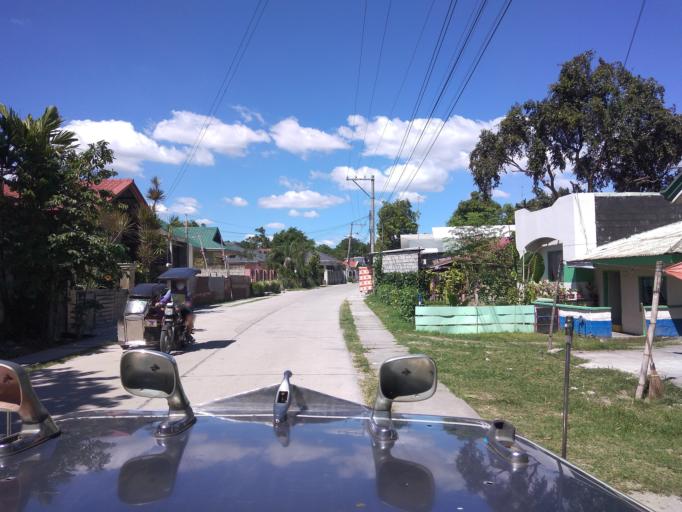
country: PH
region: Central Luzon
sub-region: Province of Pampanga
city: Magliman
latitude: 15.0351
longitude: 120.6473
